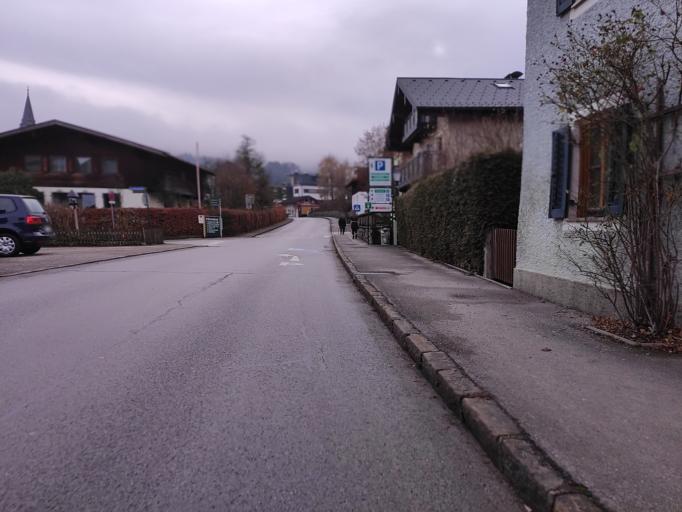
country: AT
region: Salzburg
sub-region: Politischer Bezirk Salzburg-Umgebung
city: Mattsee
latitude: 47.9727
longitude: 13.1028
